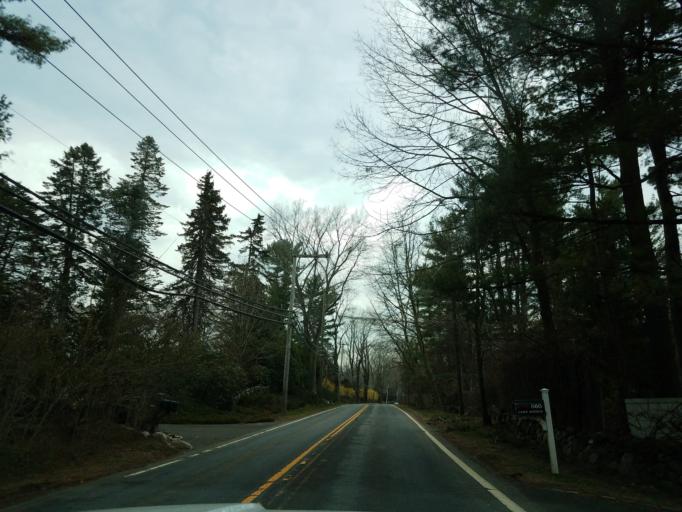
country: US
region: Connecticut
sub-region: Fairfield County
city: Glenville
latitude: 41.0602
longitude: -73.6393
